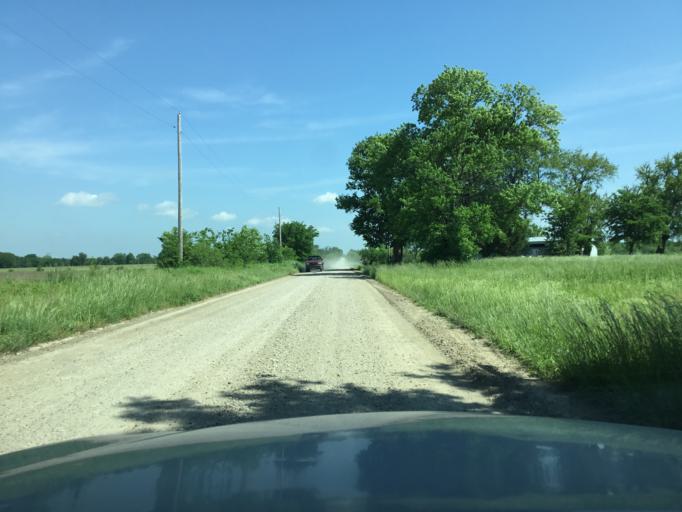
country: US
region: Kansas
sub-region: Labette County
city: Oswego
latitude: 37.1895
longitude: -95.1400
